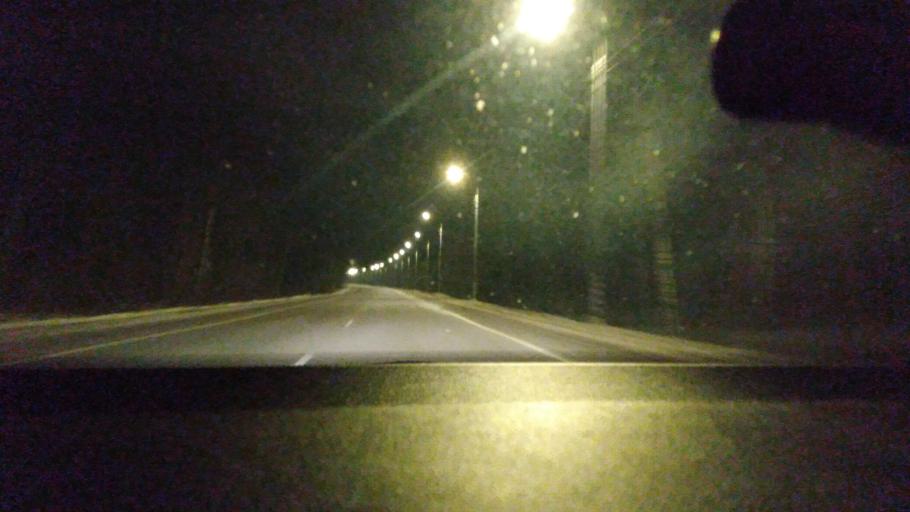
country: RU
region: Moskovskaya
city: Il'inskiy Pogost
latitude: 55.4728
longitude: 38.9574
